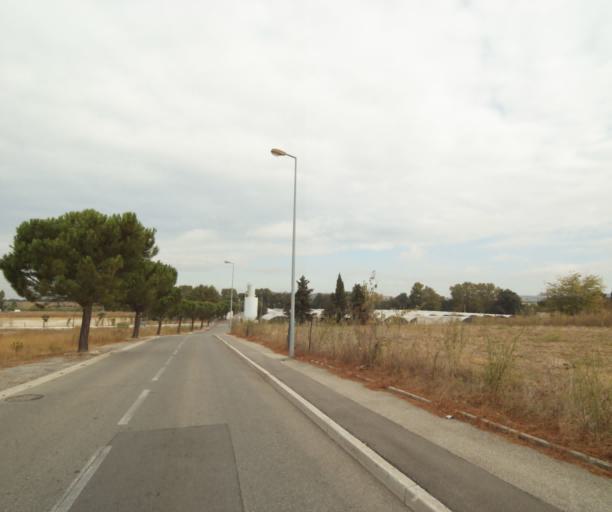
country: FR
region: Provence-Alpes-Cote d'Azur
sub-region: Departement des Bouches-du-Rhone
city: Saint-Victoret
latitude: 43.4136
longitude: 5.2658
